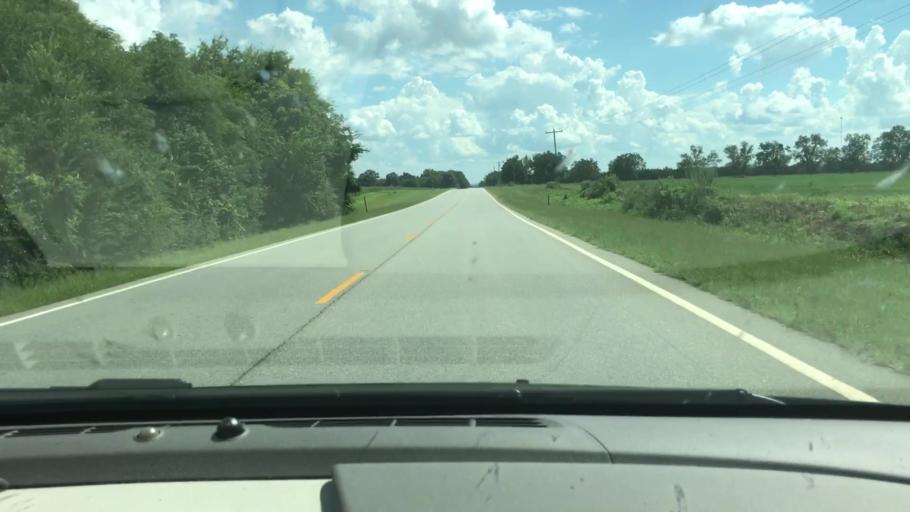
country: US
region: Georgia
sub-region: Quitman County
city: Georgetown
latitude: 31.8094
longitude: -85.0933
